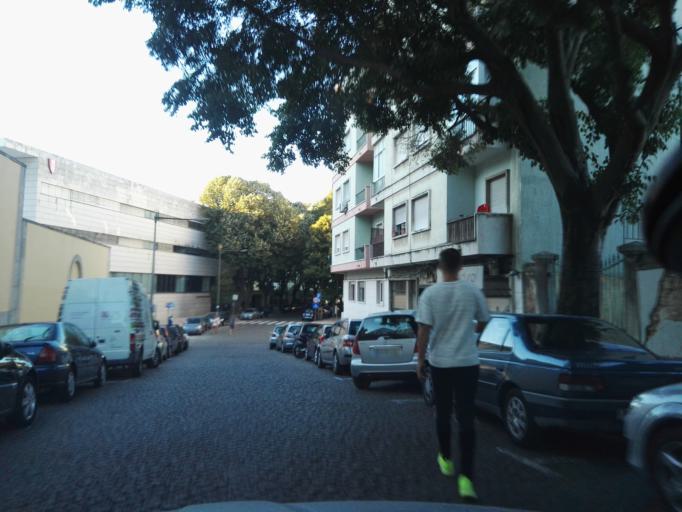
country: PT
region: Lisbon
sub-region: Lisbon
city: Lisbon
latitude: 38.7101
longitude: -9.1547
